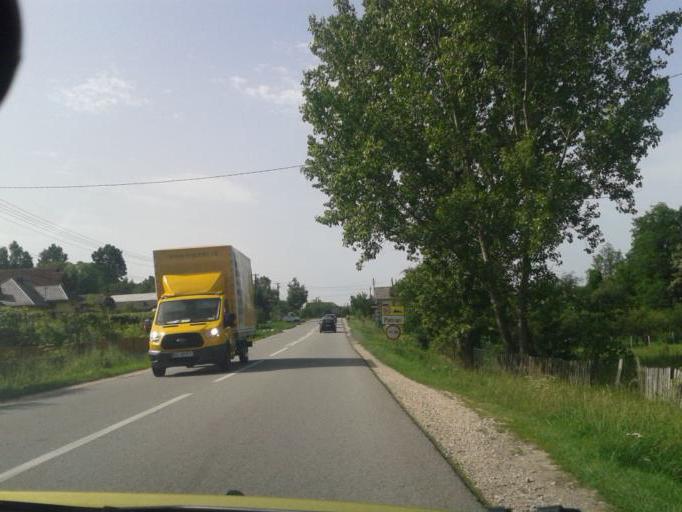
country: RO
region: Valcea
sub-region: Comuna Barbatesti
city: Bodesti
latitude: 45.1223
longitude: 24.1156
